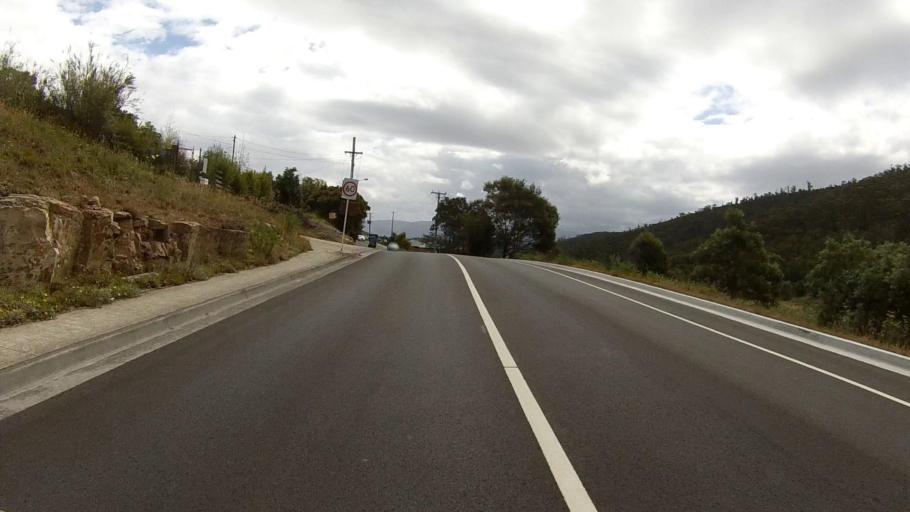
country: AU
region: Tasmania
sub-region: Clarence
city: Warrane
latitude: -42.8575
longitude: 147.4096
